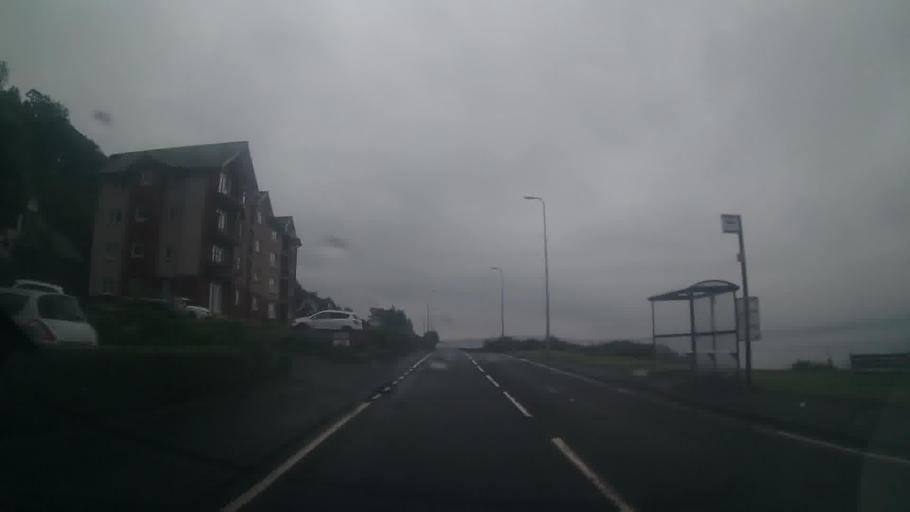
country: GB
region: Scotland
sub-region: North Ayrshire
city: Skelmorlie
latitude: 55.8652
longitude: -4.8910
